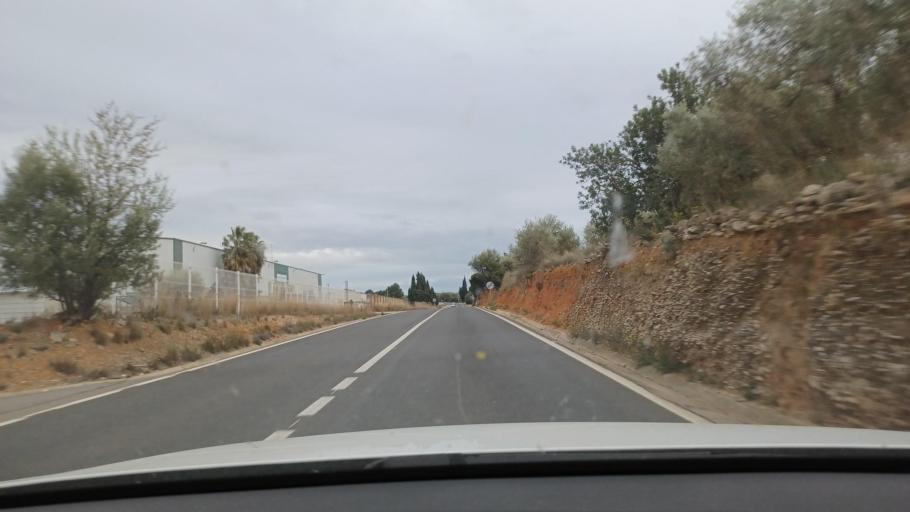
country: ES
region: Catalonia
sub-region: Provincia de Tarragona
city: Masdenverge
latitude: 40.7105
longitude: 0.5375
